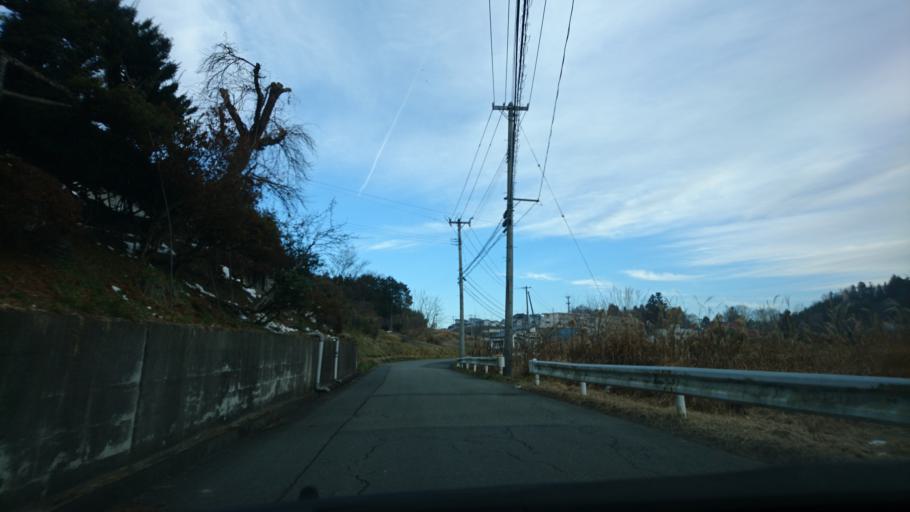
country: JP
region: Iwate
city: Ichinoseki
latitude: 38.9090
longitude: 141.3400
